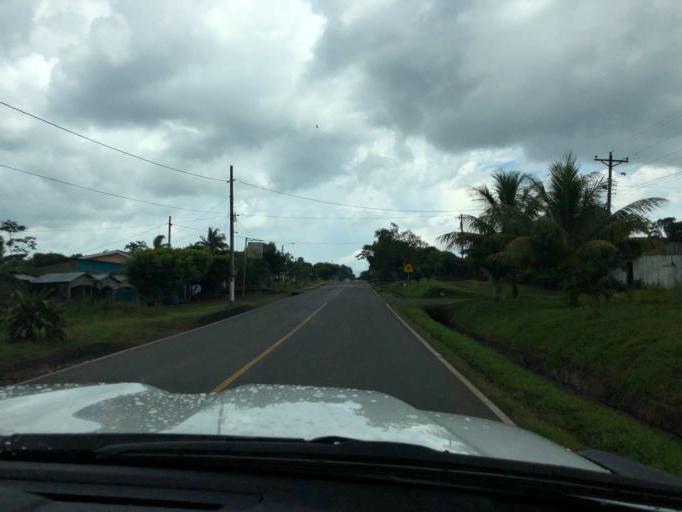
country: NI
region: Chontales
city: Villa Sandino
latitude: 11.9952
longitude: -84.8722
